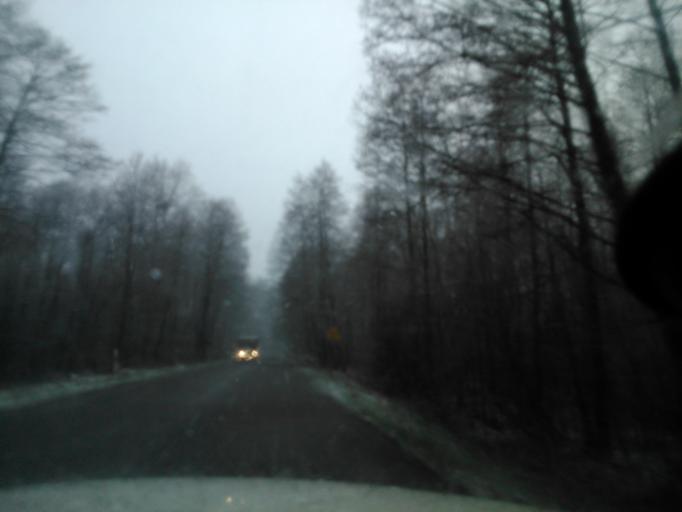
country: PL
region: Warmian-Masurian Voivodeship
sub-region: Powiat dzialdowski
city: Rybno
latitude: 53.3291
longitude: 19.9395
